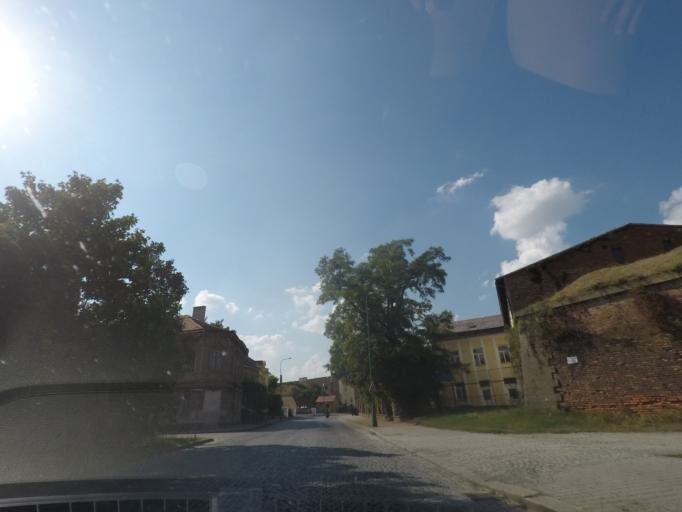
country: CZ
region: Kralovehradecky
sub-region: Okres Nachod
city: Jaromer
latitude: 50.3364
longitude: 15.9332
